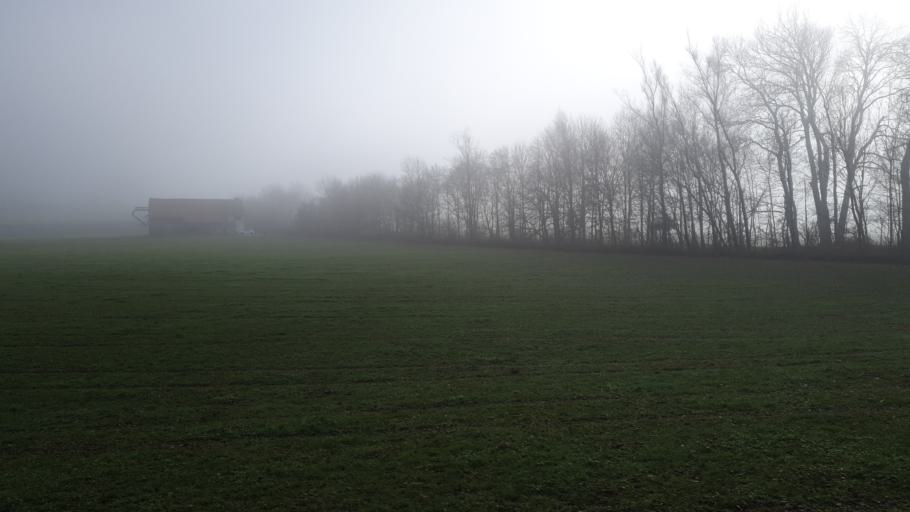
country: CH
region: Fribourg
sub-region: Veveyse District
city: Chatel-Saint-Denis
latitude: 46.5600
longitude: 6.9118
